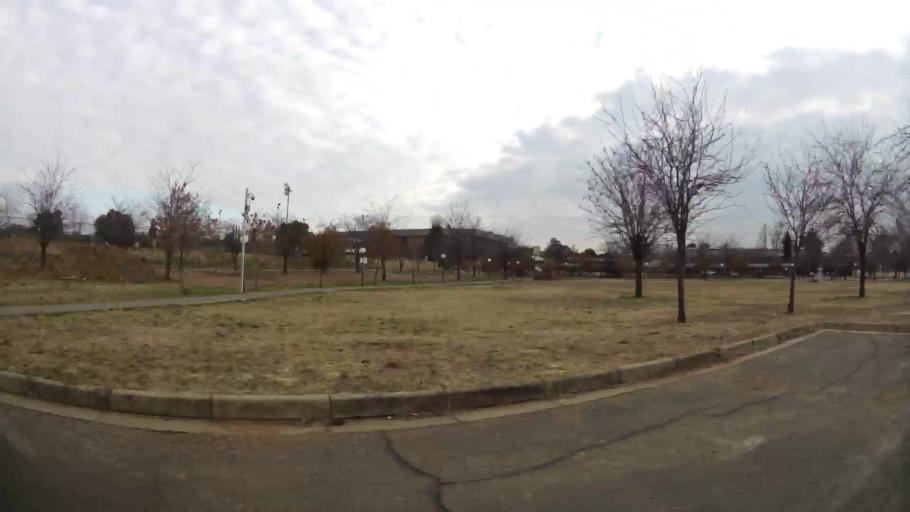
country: ZA
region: Orange Free State
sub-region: Mangaung Metropolitan Municipality
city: Bloemfontein
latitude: -29.1148
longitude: 26.1892
